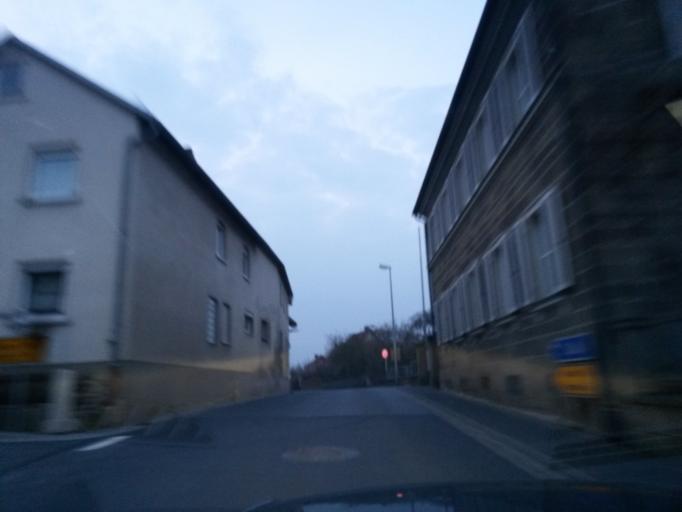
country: DE
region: Bavaria
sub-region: Regierungsbezirk Unterfranken
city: Massbach
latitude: 50.1848
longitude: 10.2751
